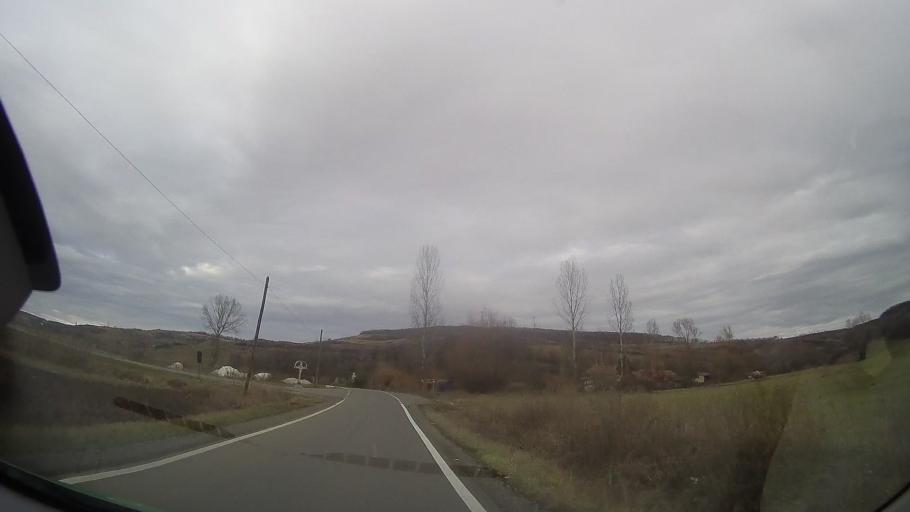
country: RO
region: Mures
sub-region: Comuna Cozma
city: Cozma
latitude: 46.7944
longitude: 24.5425
